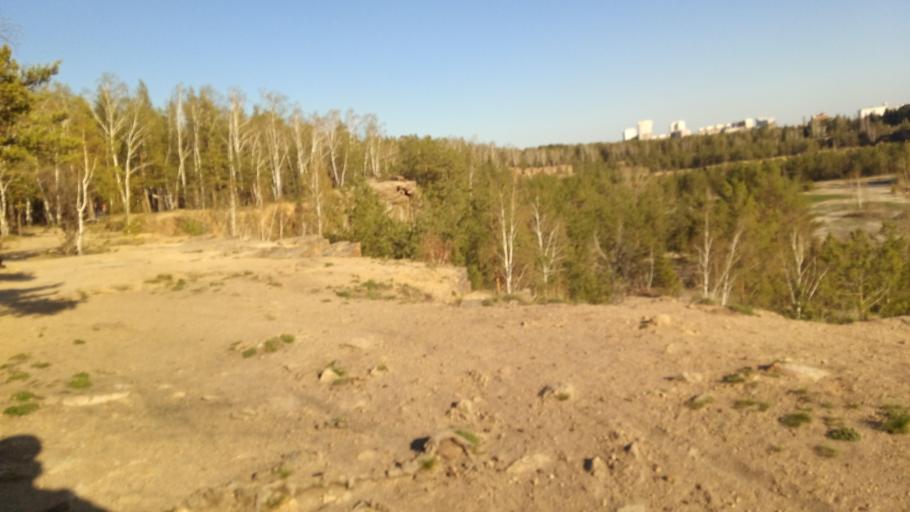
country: RU
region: Chelyabinsk
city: Novosineglazovskiy
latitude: 55.1256
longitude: 61.3339
